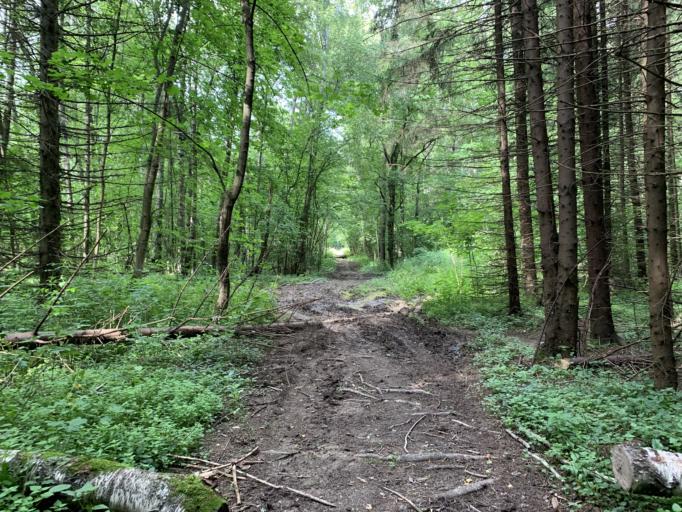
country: RU
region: Moskovskaya
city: Podosinki
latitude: 56.1806
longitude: 37.5678
